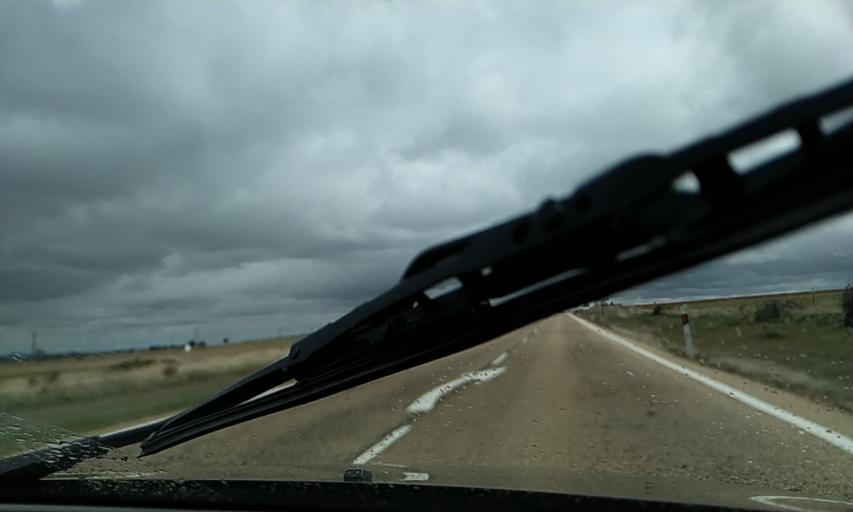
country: ES
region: Castille and Leon
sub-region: Provincia de Zamora
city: Tabara
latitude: 41.8500
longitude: -5.9858
